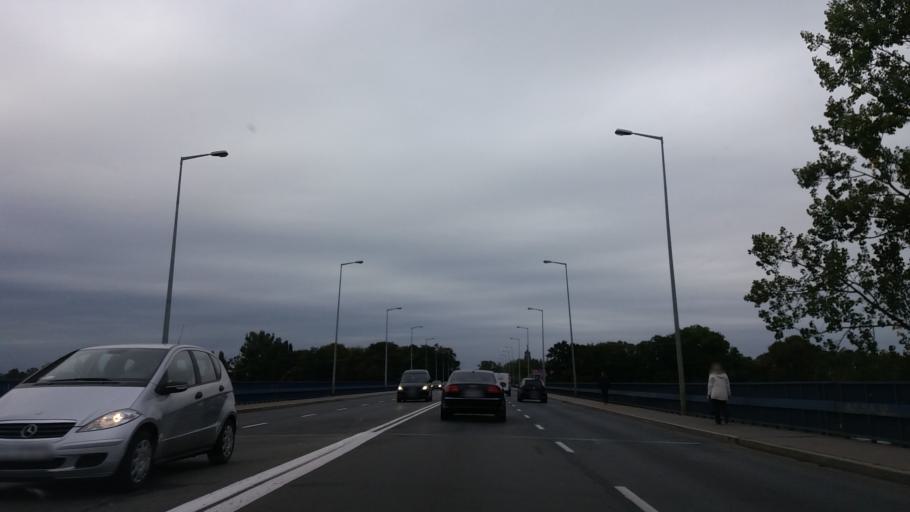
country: PL
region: Lubusz
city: Gorzow Wielkopolski
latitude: 52.7318
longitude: 15.2551
